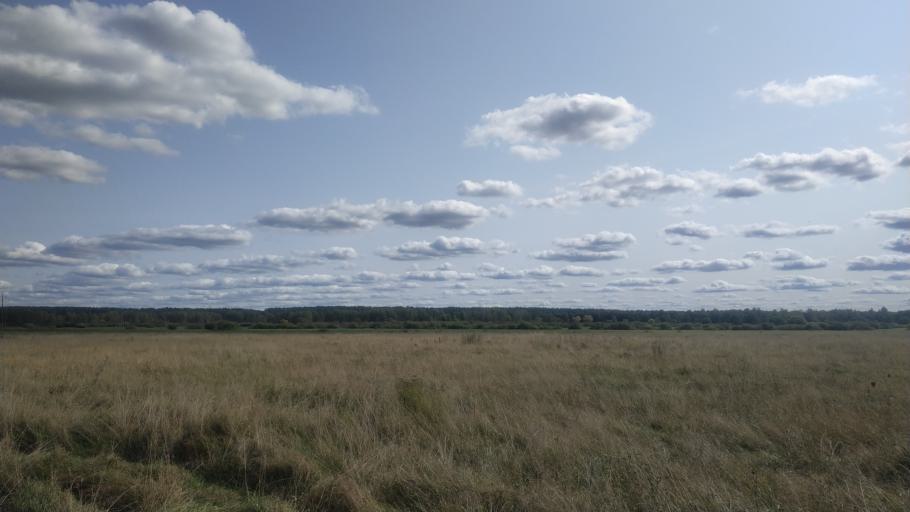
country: RU
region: Brjansk
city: Zhukovka
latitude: 53.5245
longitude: 33.6613
